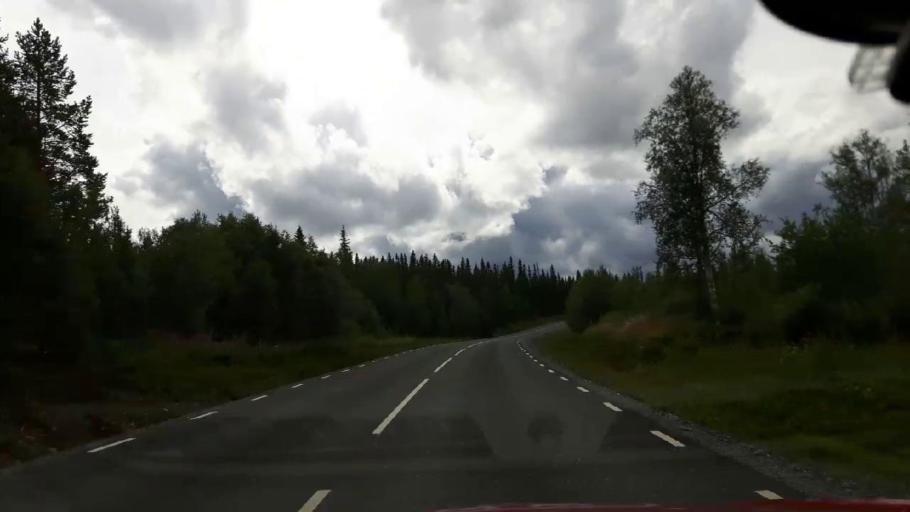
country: NO
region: Nord-Trondelag
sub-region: Lierne
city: Sandvika
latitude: 64.5984
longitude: 14.1203
